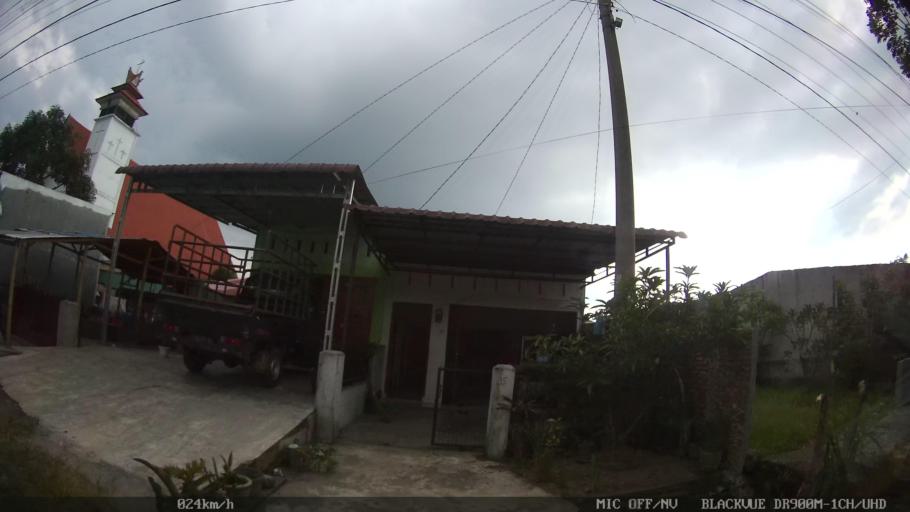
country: ID
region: North Sumatra
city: Sunggal
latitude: 3.5218
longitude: 98.6175
